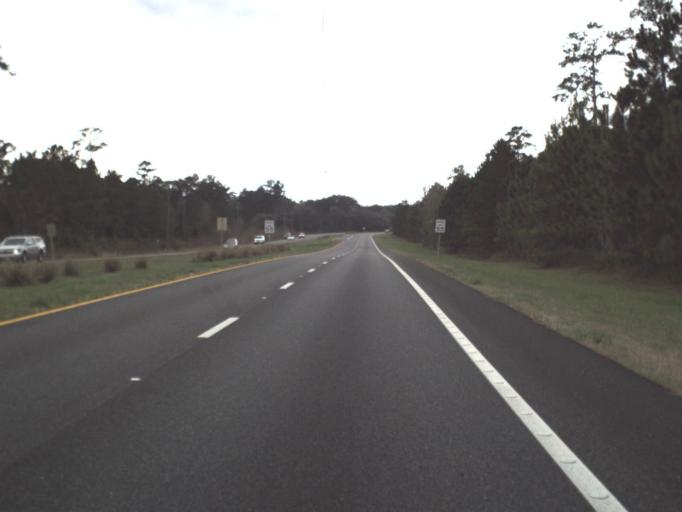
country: US
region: Florida
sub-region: Leon County
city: Tallahassee
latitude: 30.5819
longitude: -84.1984
